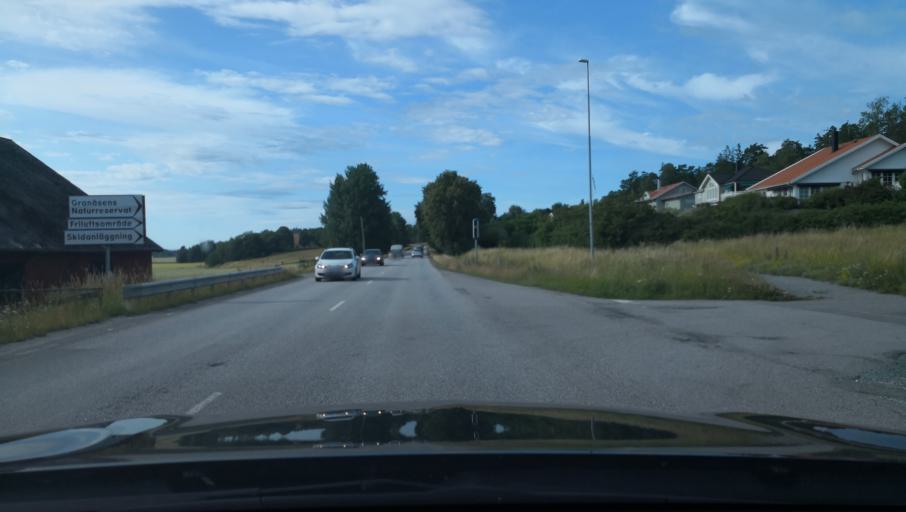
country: SE
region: Uppsala
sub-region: Habo Kommun
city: Balsta
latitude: 59.5956
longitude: 17.5104
